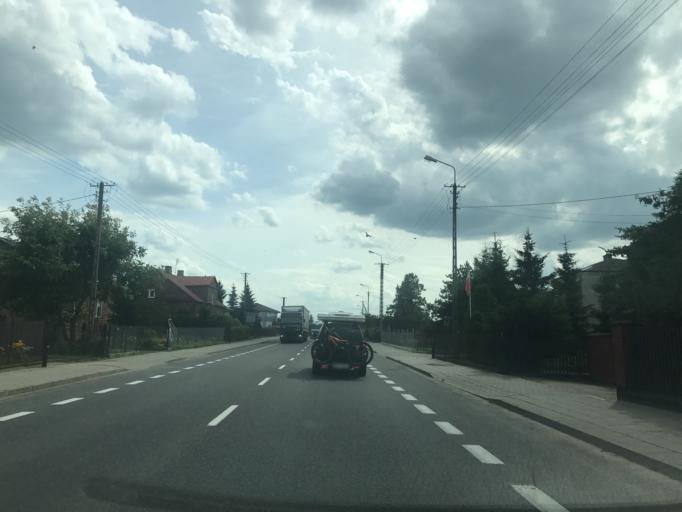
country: PL
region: Masovian Voivodeship
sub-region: Powiat mlawski
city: Wisniewo
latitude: 53.0625
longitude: 20.3473
